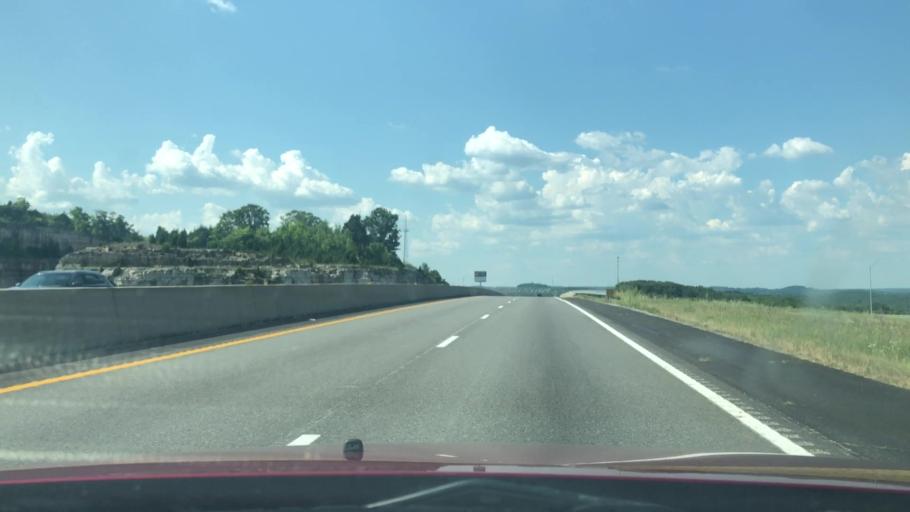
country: US
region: Missouri
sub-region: Taney County
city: Merriam Woods
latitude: 36.7102
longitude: -93.2208
